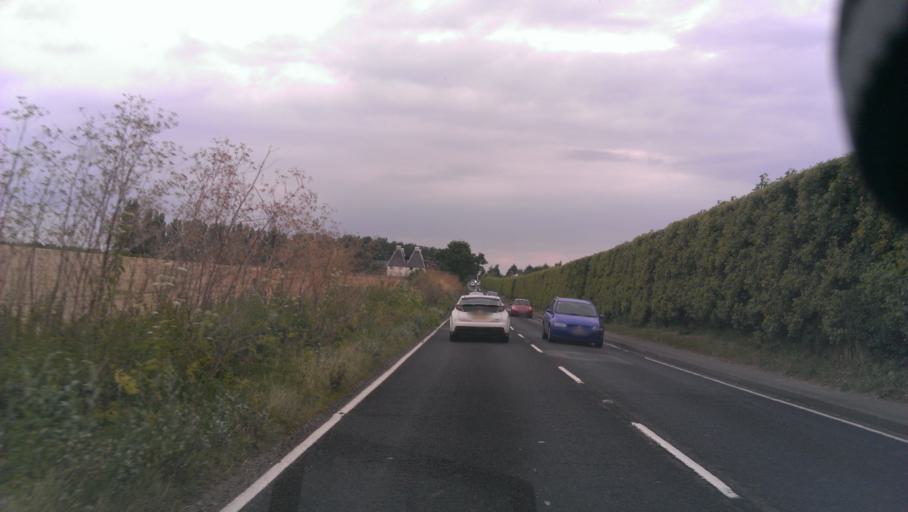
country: GB
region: England
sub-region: Kent
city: Faversham
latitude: 51.3031
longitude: 0.9175
